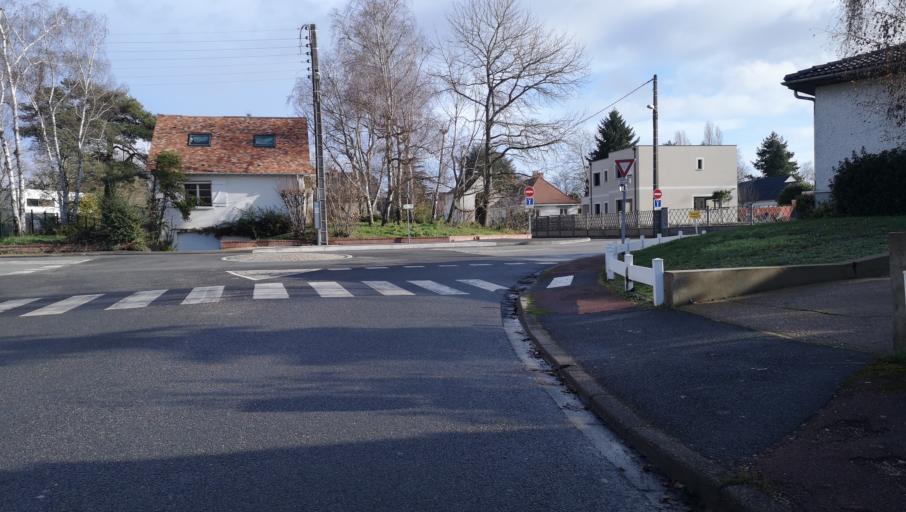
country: FR
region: Centre
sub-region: Departement du Loiret
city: Saint-Pryve-Saint-Mesmin
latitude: 47.8872
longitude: 1.8763
